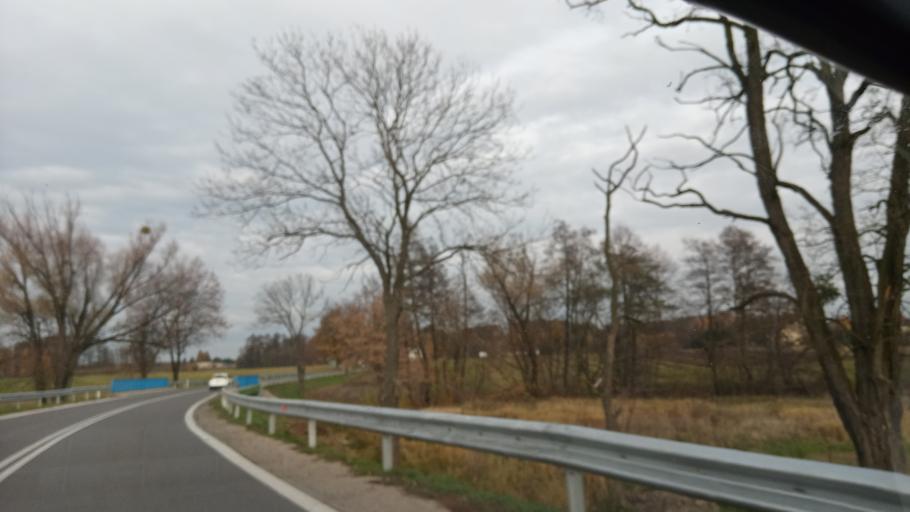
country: PL
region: Lodz Voivodeship
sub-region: Powiat skierniewicki
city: Bolimow
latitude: 52.1603
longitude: 20.1768
